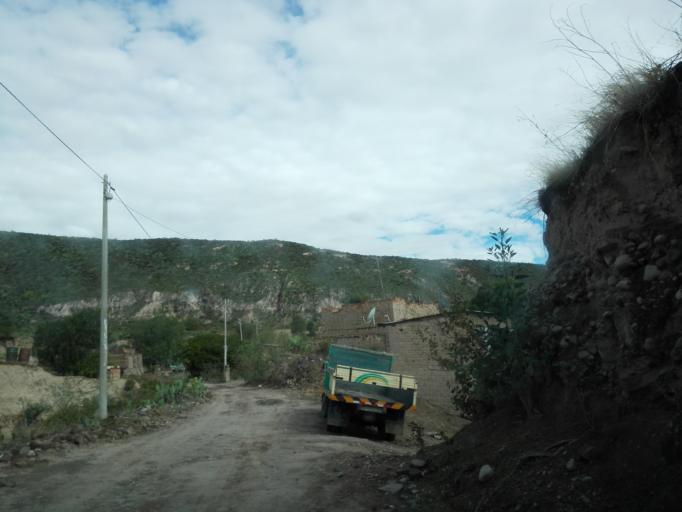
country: PE
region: Ayacucho
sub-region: Provincia de Huamanga
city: Pacaycasa
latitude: -13.0651
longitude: -74.2504
